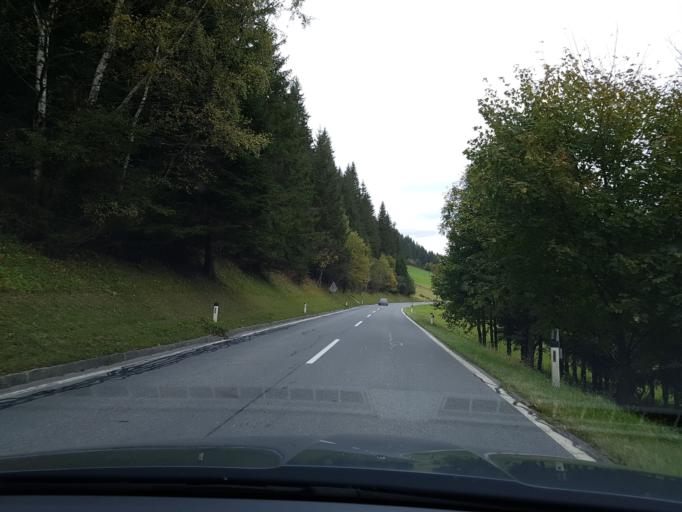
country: AT
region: Salzburg
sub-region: Politischer Bezirk Tamsweg
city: Tamsweg
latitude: 47.1086
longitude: 13.8163
